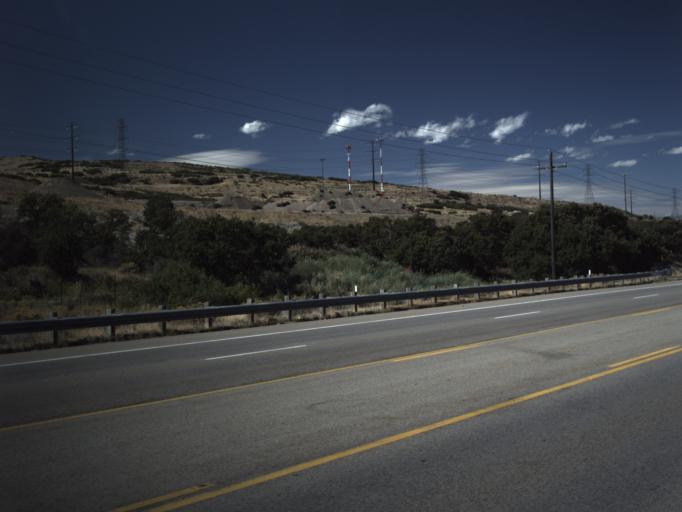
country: US
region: Utah
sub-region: Salt Lake County
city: Bluffdale
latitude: 40.4494
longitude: -111.9366
